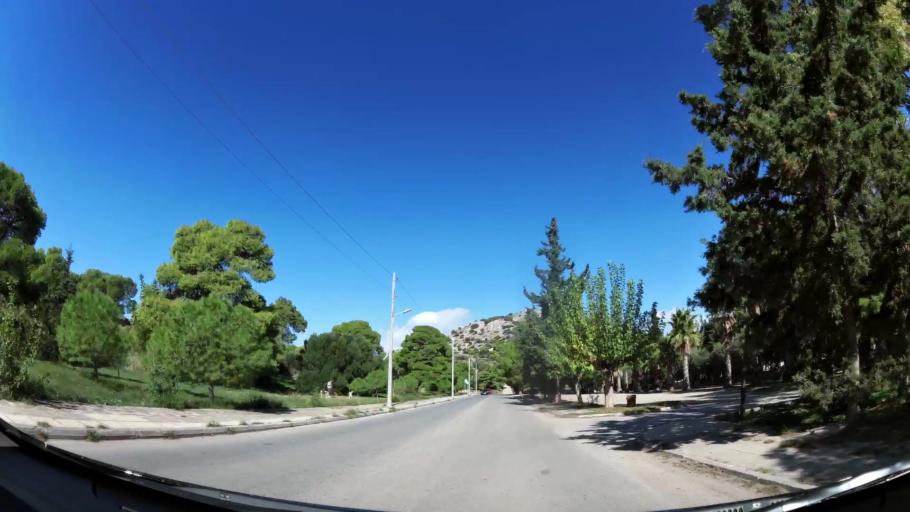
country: GR
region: Attica
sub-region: Nomarchia Anatolikis Attikis
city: Vouliagmeni
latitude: 37.8139
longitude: 23.7901
